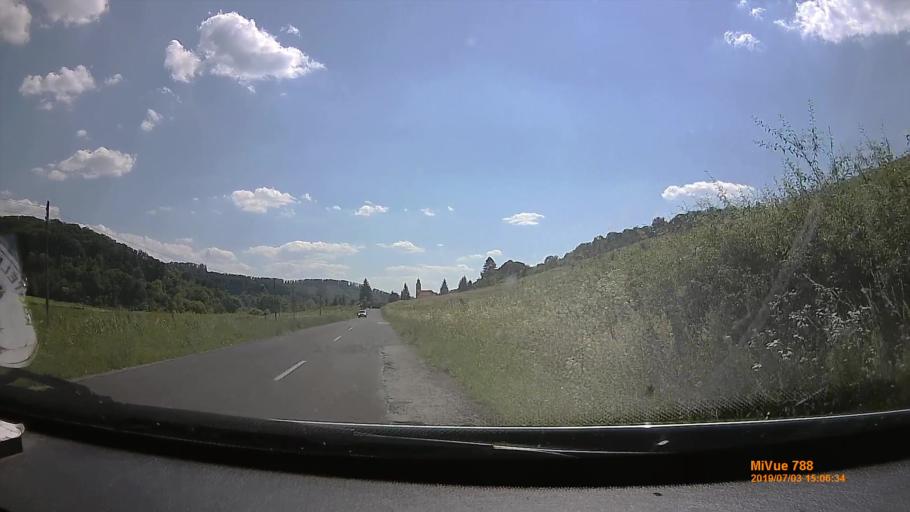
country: HU
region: Borsod-Abauj-Zemplen
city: Putnok
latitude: 48.2585
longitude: 20.3962
